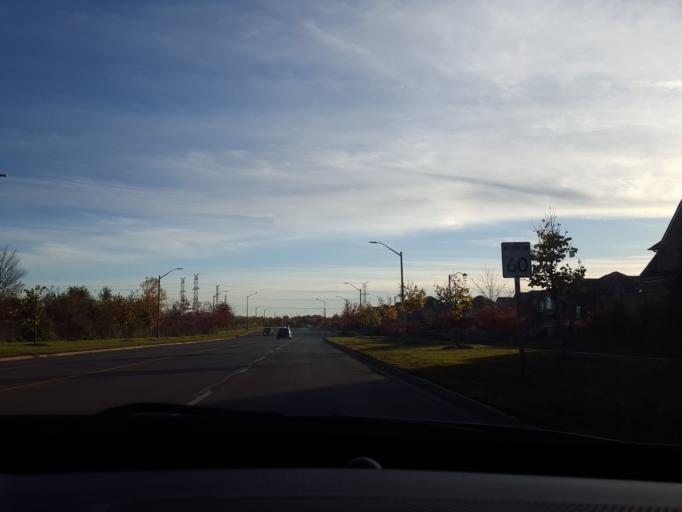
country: CA
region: Ontario
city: Markham
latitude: 43.8545
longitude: -79.2220
